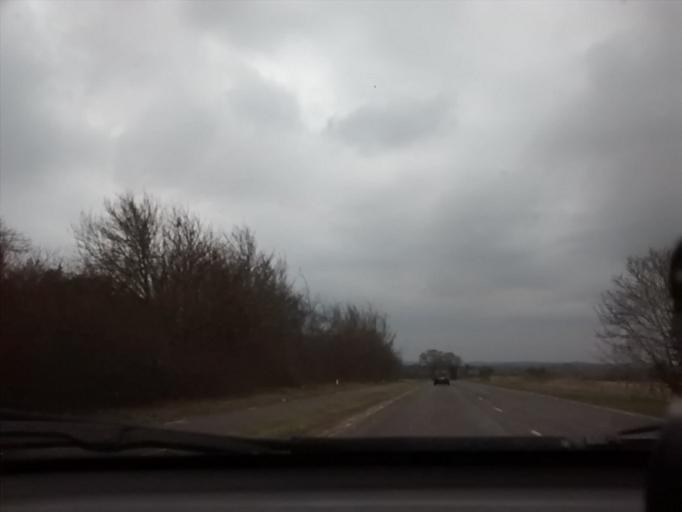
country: GB
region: England
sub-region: Cambridgeshire
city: Sawston
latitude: 52.1500
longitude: 0.1907
